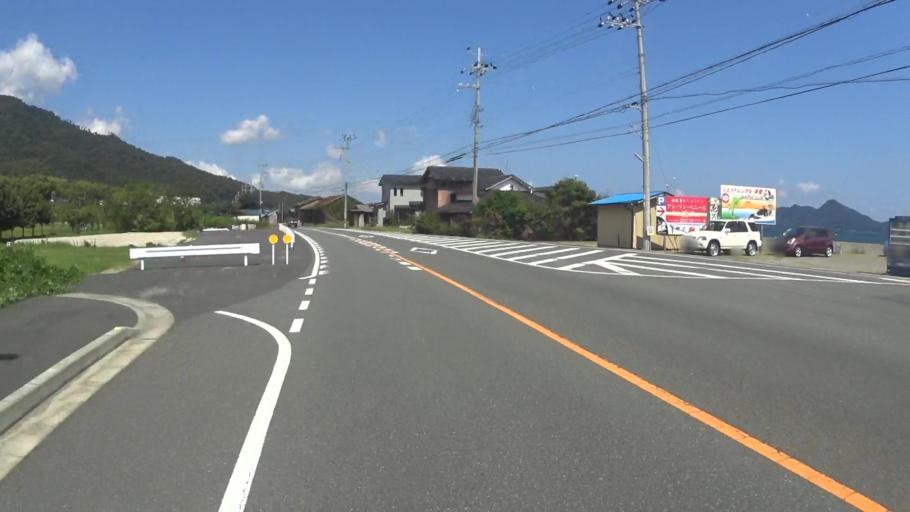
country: JP
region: Kyoto
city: Miyazu
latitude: 35.5852
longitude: 135.2056
